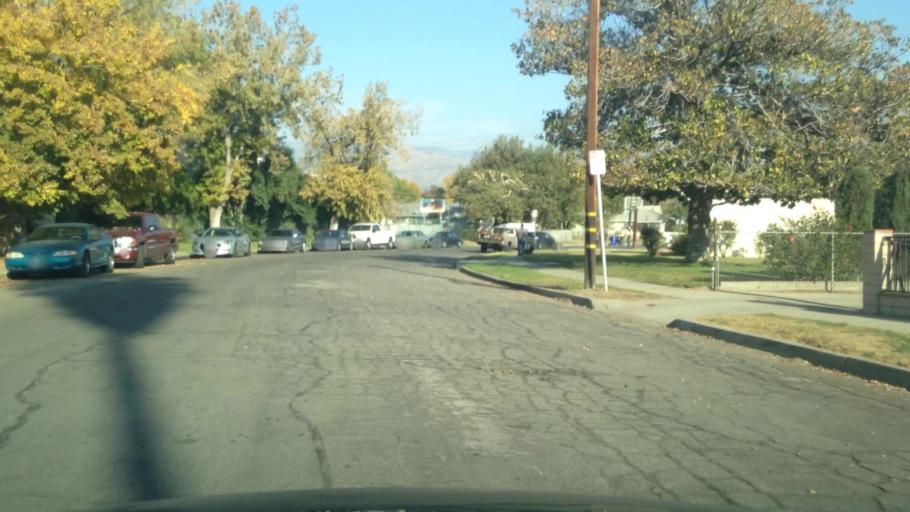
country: US
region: California
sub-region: San Bernardino County
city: San Bernardino
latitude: 34.1238
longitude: -117.2762
